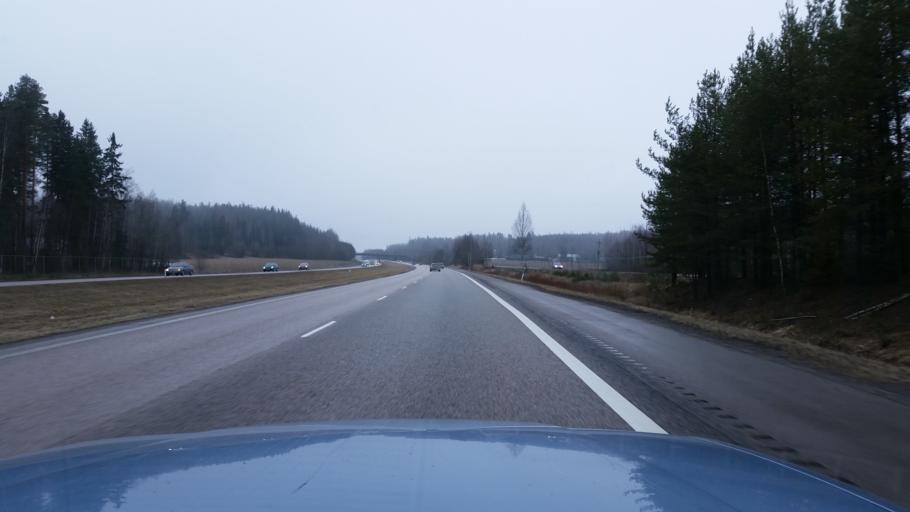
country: FI
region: Uusimaa
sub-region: Helsinki
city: Nurmijaervi
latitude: 60.4273
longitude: 24.8265
